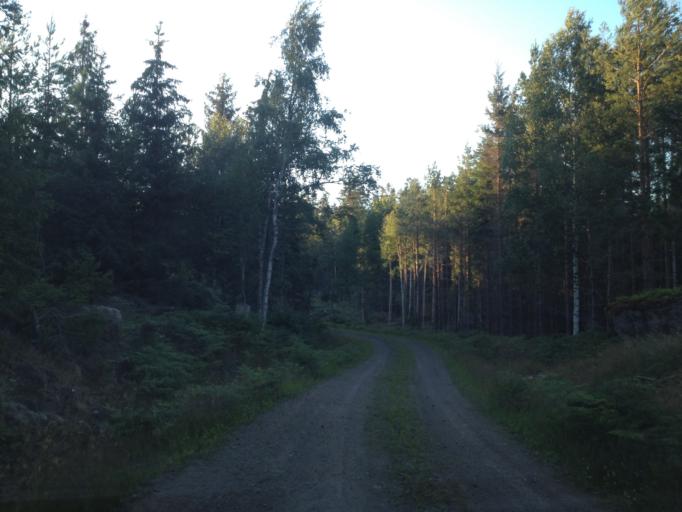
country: SE
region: Kalmar
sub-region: Vasterviks Kommun
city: Overum
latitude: 57.9958
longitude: 16.1688
